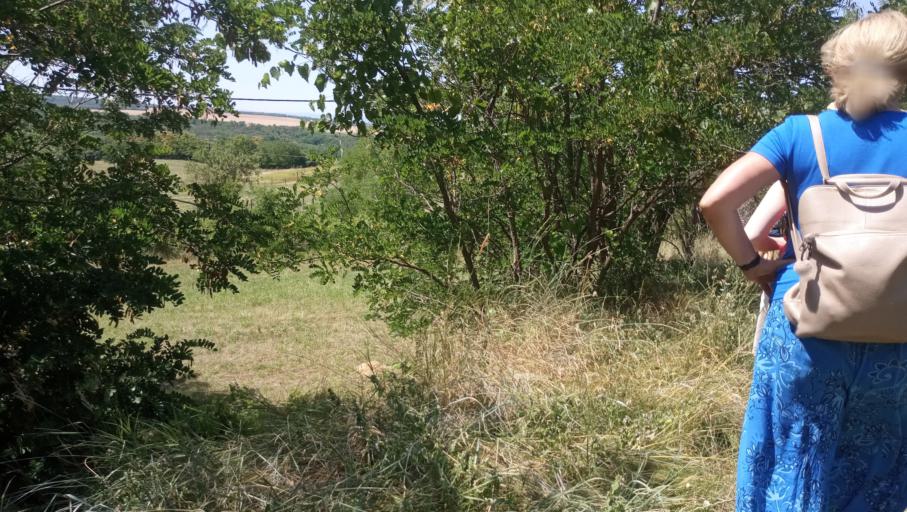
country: HU
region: Somogy
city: Siofok
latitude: 46.8288
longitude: 18.0846
